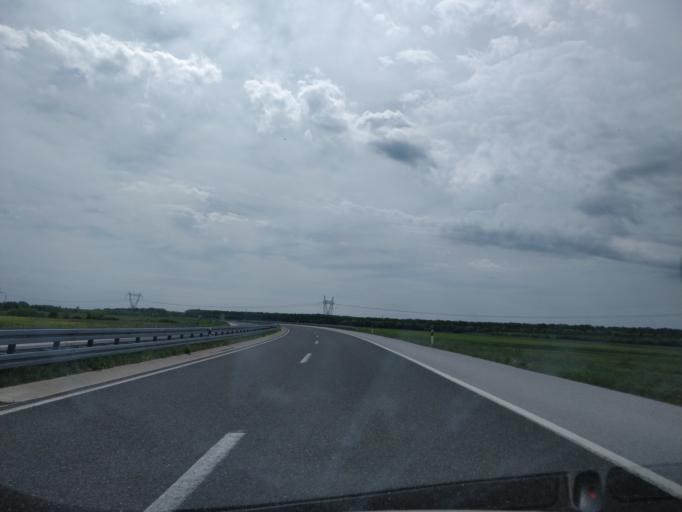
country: HR
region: Zagrebacka
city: Mraclin
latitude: 45.6534
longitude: 16.0762
